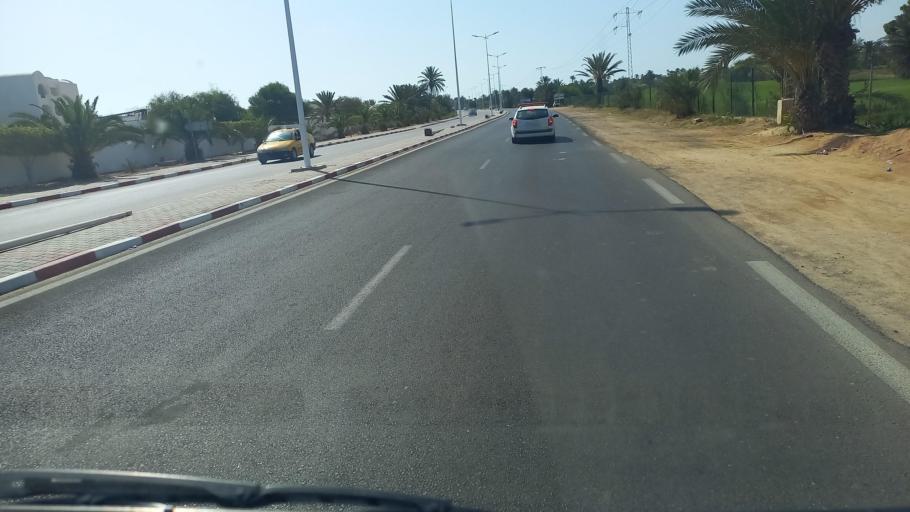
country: TN
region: Madanin
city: Midoun
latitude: 33.8342
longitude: 11.0030
